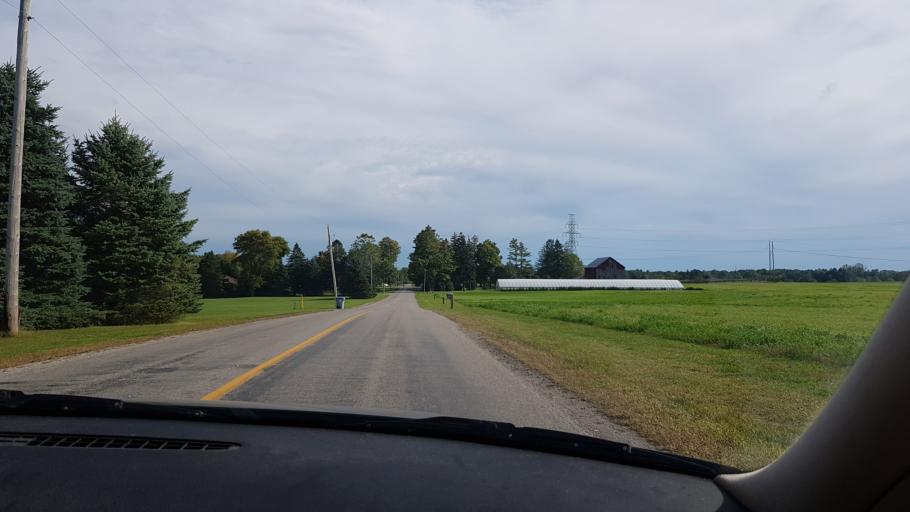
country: CA
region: Ontario
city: Delaware
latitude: 42.8970
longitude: -81.4716
